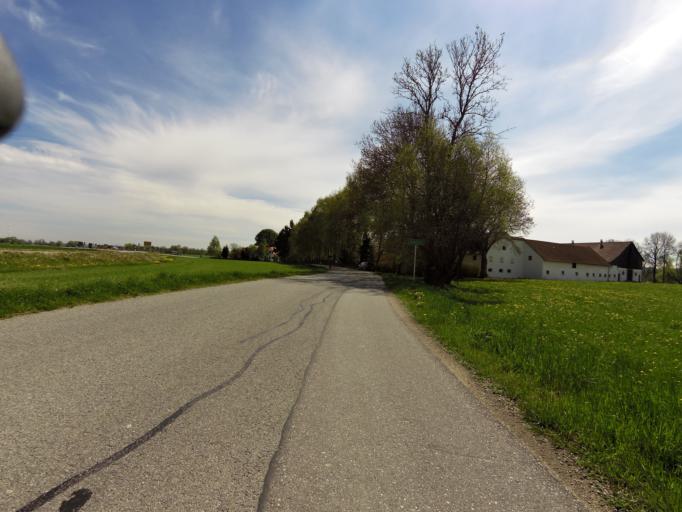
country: DE
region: Bavaria
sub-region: Lower Bavaria
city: Bruckberg
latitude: 48.5164
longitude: 12.0299
